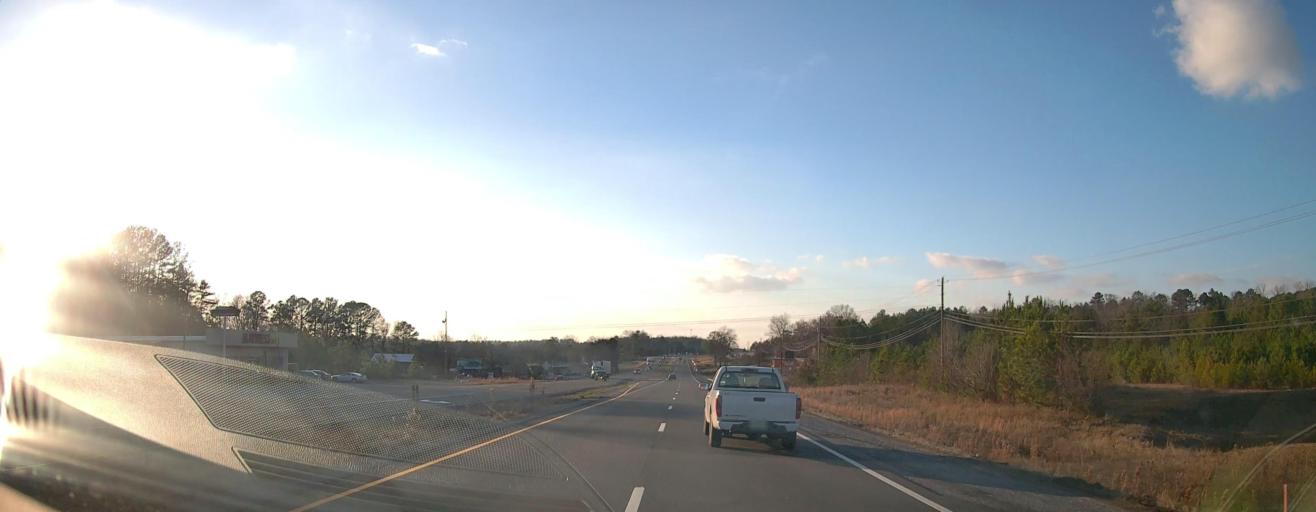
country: US
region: Alabama
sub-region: Calhoun County
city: Saks
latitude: 33.7157
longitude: -85.8578
